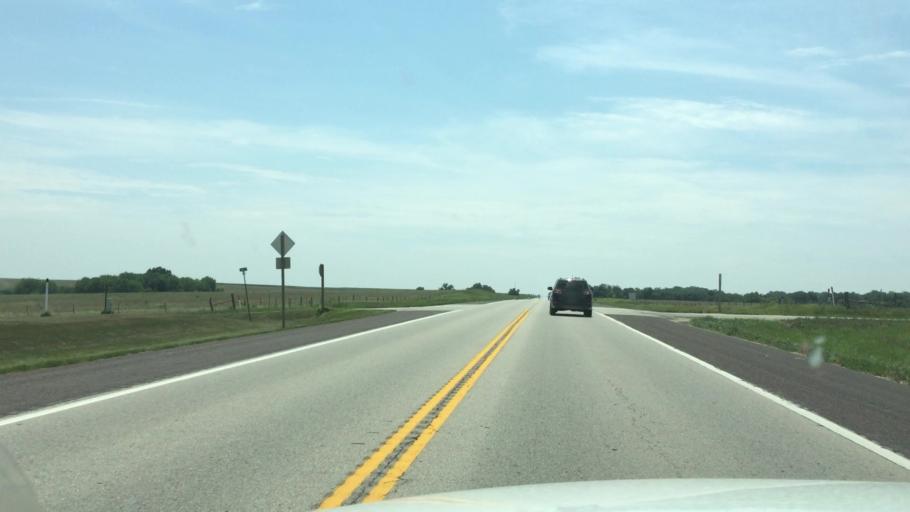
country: US
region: Kansas
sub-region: Jackson County
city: Holton
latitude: 39.5218
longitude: -95.7482
